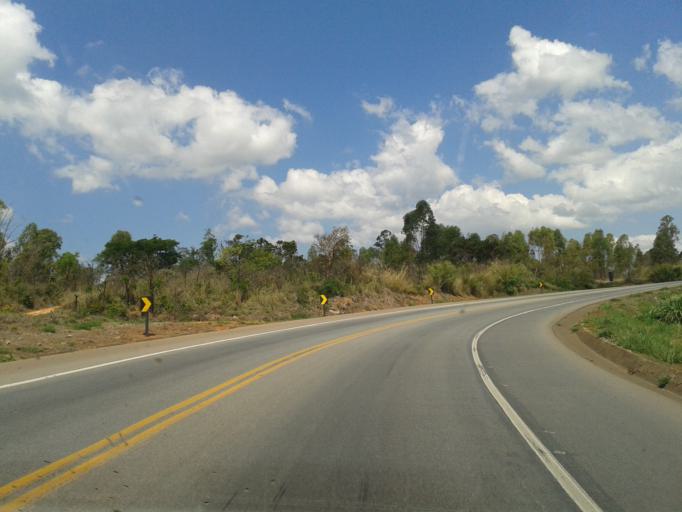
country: BR
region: Minas Gerais
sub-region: Campos Altos
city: Campos Altos
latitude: -19.6723
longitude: -46.0440
